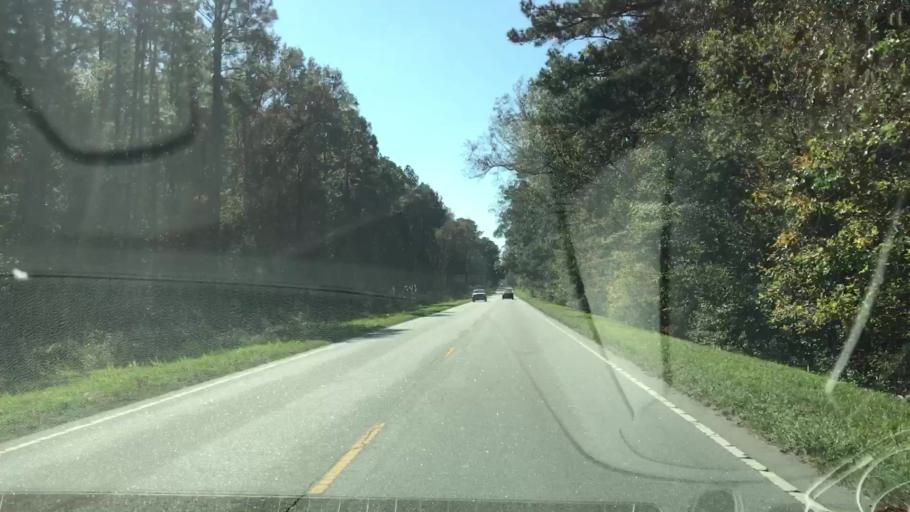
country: US
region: South Carolina
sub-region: Jasper County
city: Ridgeland
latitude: 32.4004
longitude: -80.9065
